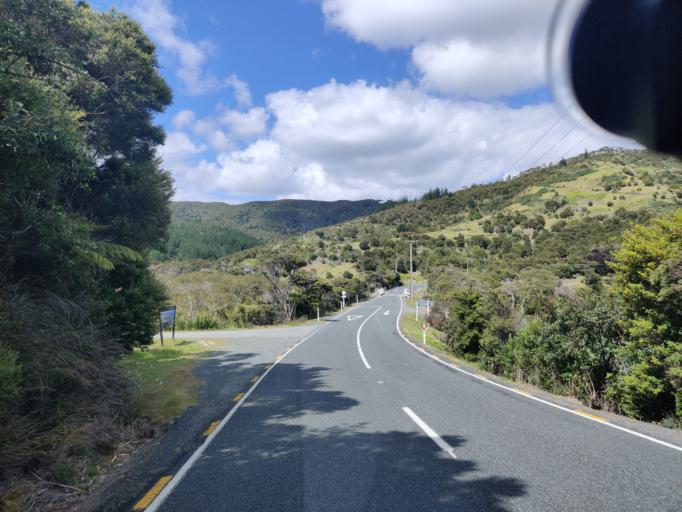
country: NZ
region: Northland
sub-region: Far North District
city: Paihia
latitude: -35.2589
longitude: 174.2314
